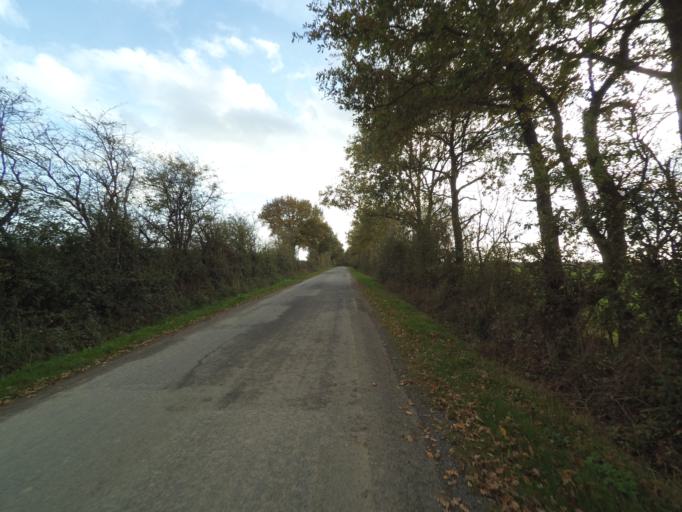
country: FR
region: Pays de la Loire
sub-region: Departement de la Vendee
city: Saint-Hilaire-de-Loulay
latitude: 47.0191
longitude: -1.3554
